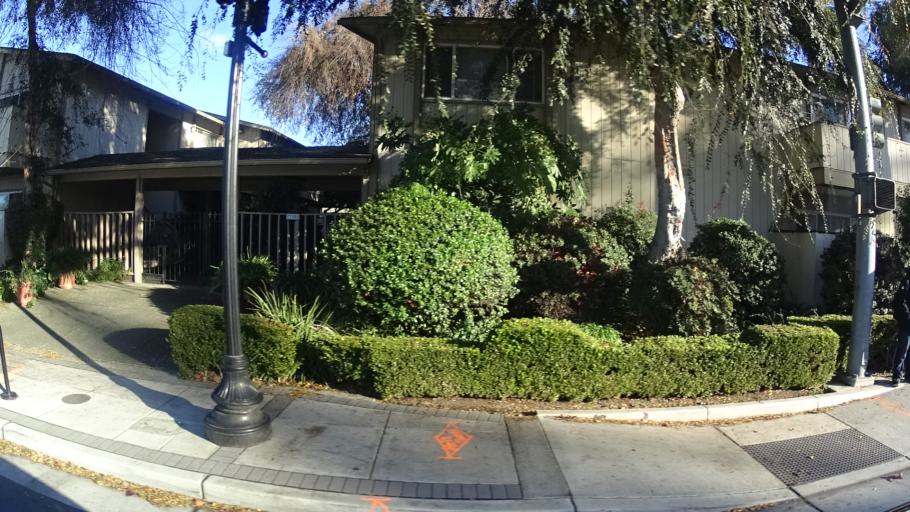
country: US
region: California
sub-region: Santa Clara County
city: Sunnyvale
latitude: 37.3726
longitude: -122.0304
